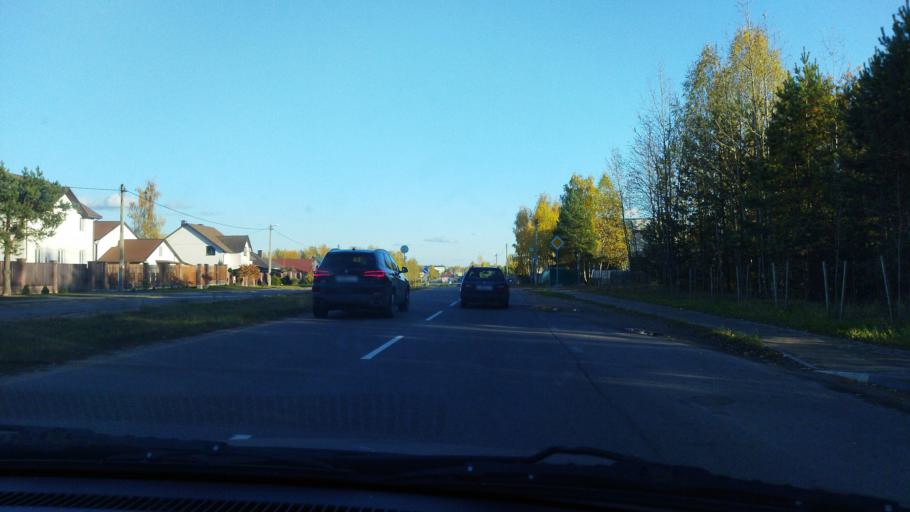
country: BY
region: Minsk
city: Kalodzishchy
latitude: 53.9178
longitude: 27.7562
